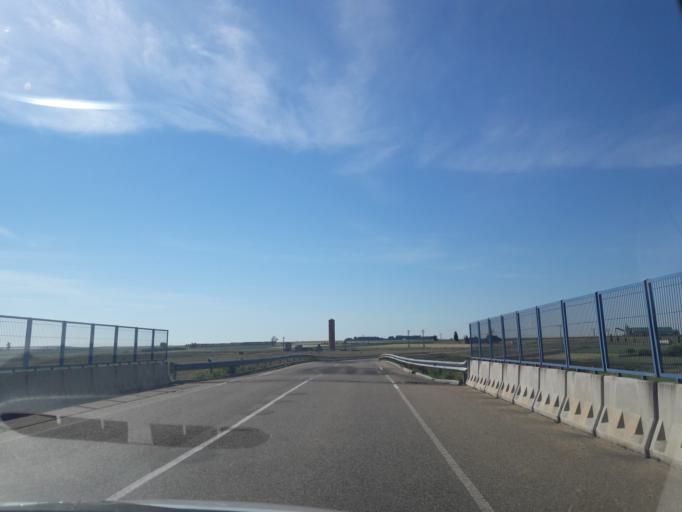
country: ES
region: Castille and Leon
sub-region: Provincia de Salamanca
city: Espino de la Orbada
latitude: 41.0837
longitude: -5.3964
